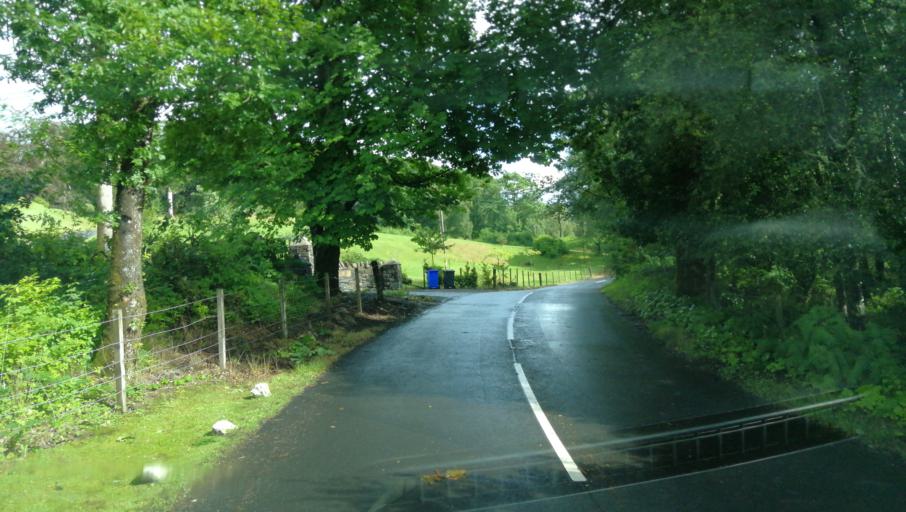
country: GB
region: Scotland
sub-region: Stirling
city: Balfron
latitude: 56.2296
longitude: -4.3935
